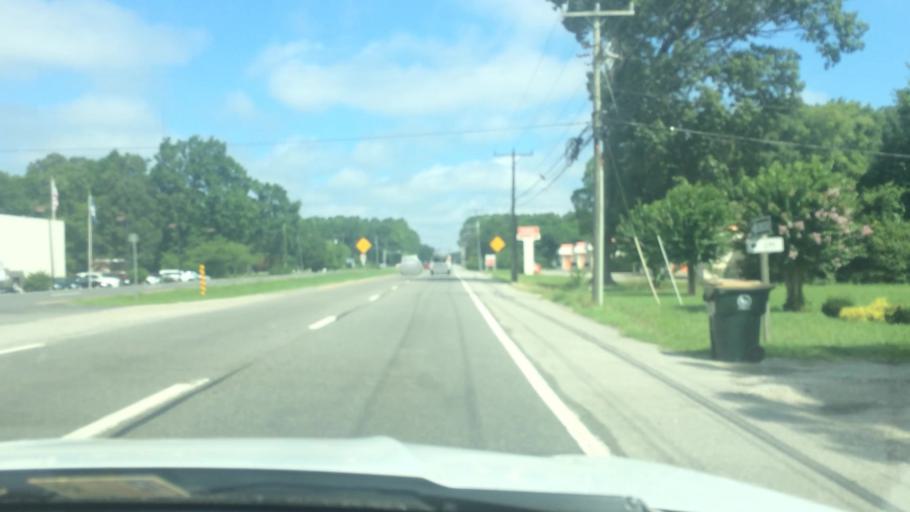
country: US
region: Virginia
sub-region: York County
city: Yorktown
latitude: 37.1817
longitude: -76.4824
